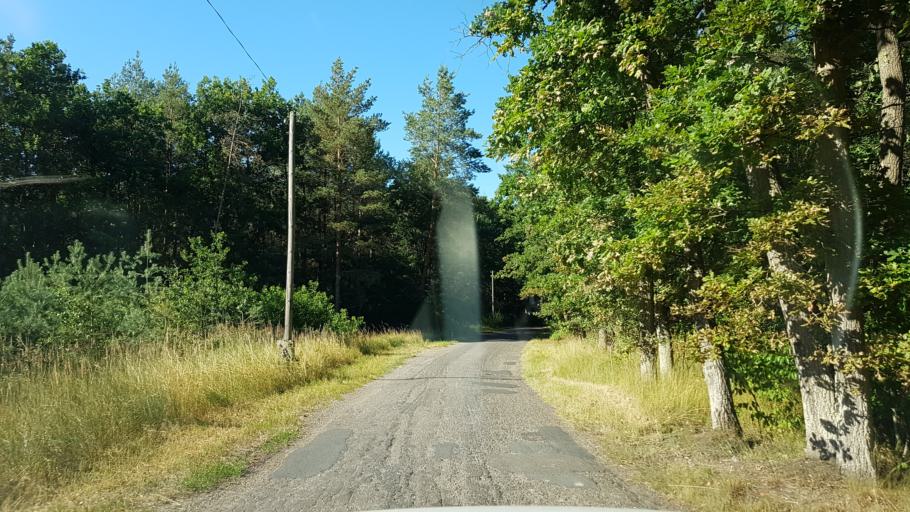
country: PL
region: West Pomeranian Voivodeship
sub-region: Powiat goleniowski
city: Goleniow
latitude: 53.5600
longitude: 14.7578
